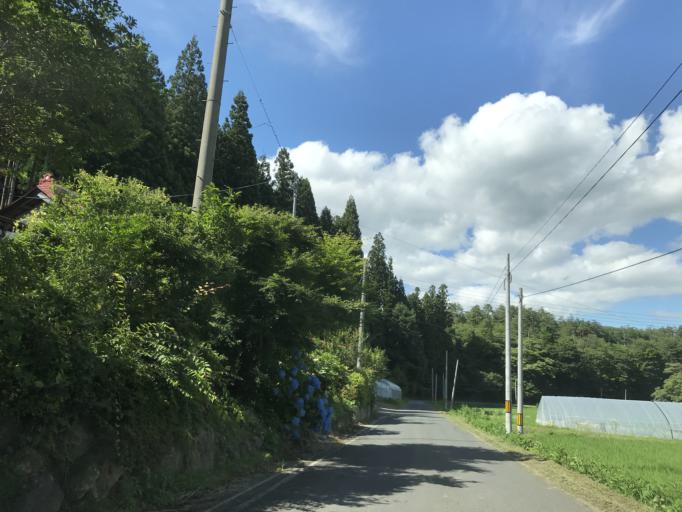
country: JP
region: Iwate
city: Ichinoseki
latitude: 38.9394
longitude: 140.9900
